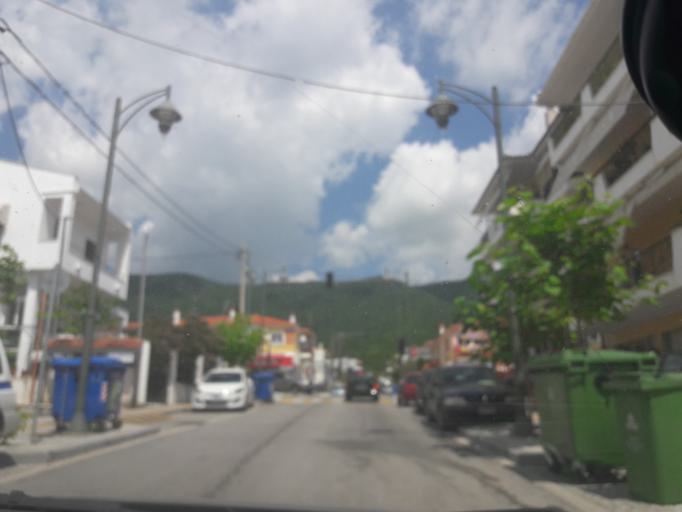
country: GR
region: Central Macedonia
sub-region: Nomos Chalkidikis
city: Polygyros
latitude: 40.3811
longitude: 23.4452
